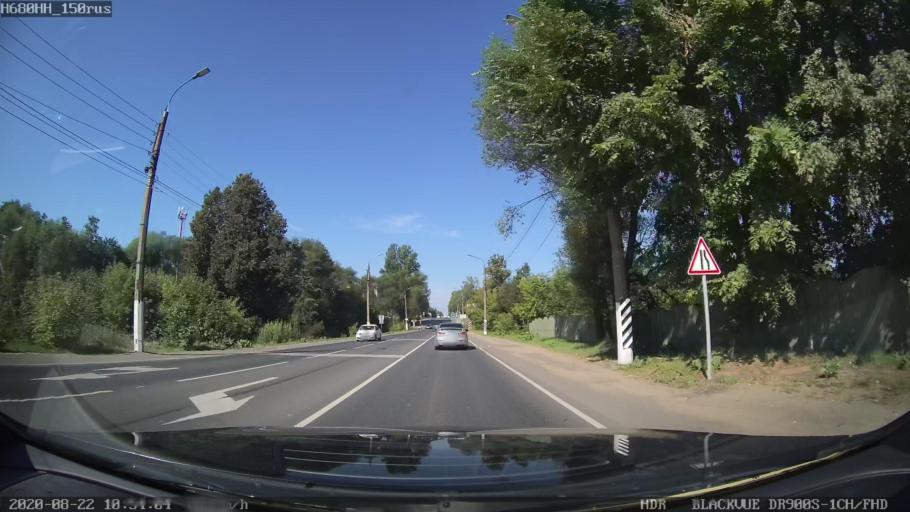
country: RU
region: Tverskaya
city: Emmaus
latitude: 56.8009
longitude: 36.0376
